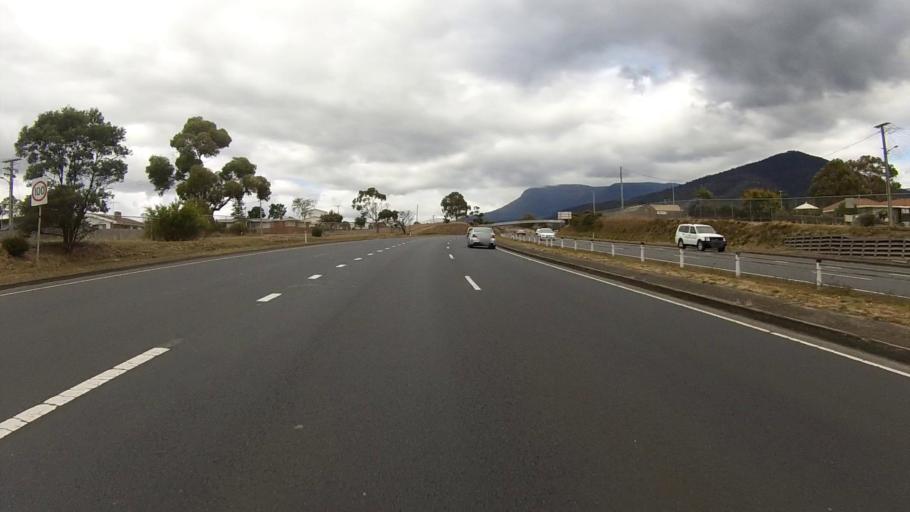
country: AU
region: Tasmania
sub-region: Glenorchy
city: Berriedale
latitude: -42.8020
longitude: 147.2498
